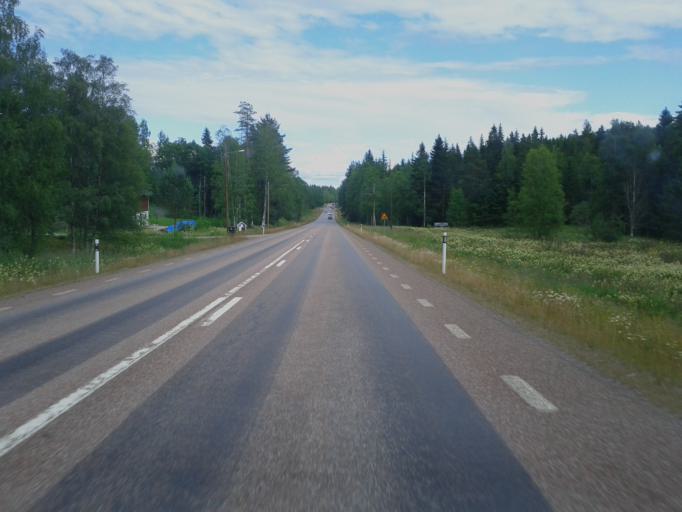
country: SE
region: Dalarna
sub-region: Faluns Kommun
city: Bjursas
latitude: 60.7410
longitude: 15.4105
